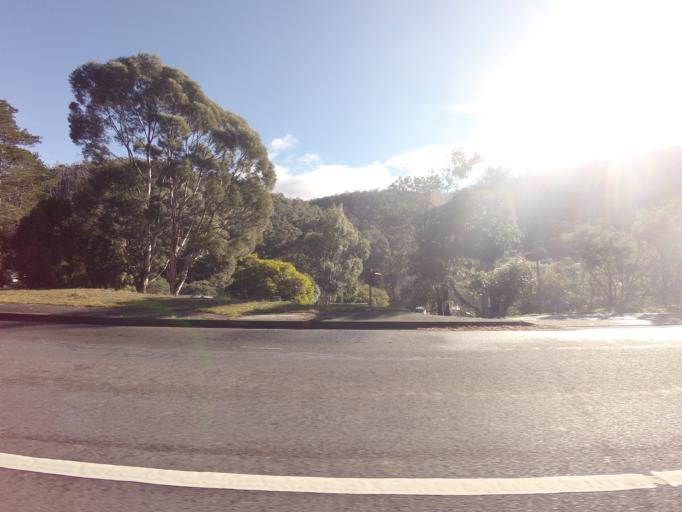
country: AU
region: Tasmania
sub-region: Glenorchy
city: Berriedale
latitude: -42.8158
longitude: 147.2275
